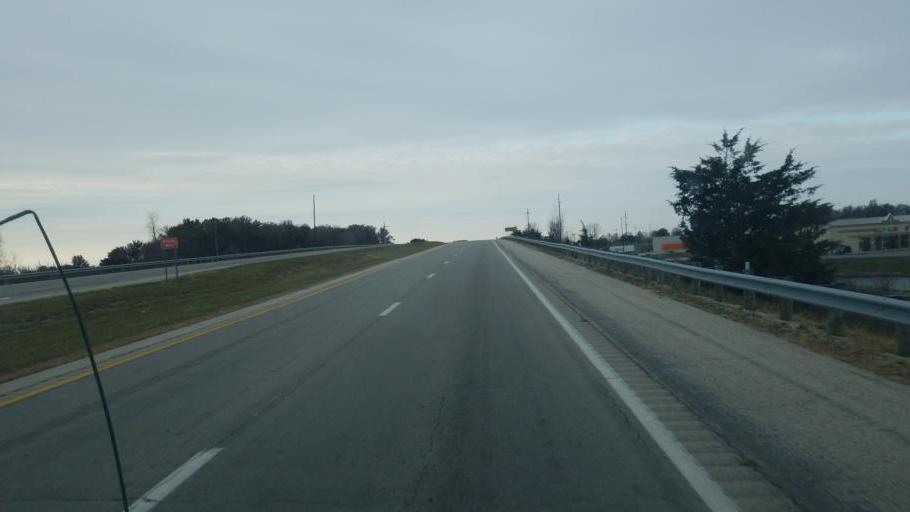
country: US
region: Ohio
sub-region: Mercer County
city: Celina
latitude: 40.5555
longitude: -84.5367
